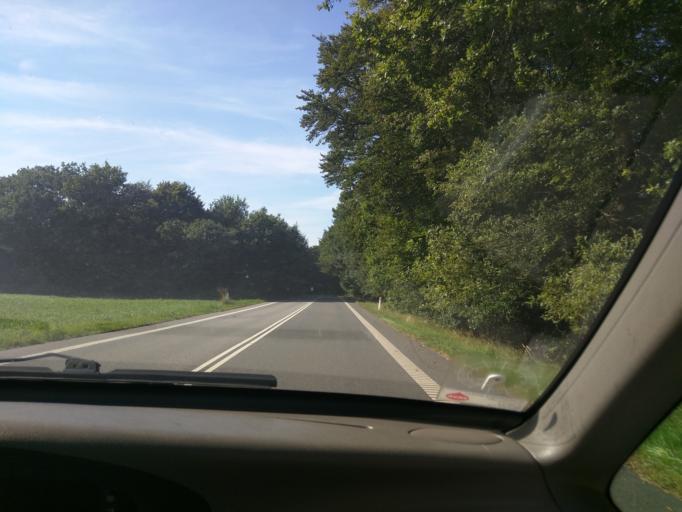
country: DK
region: Central Jutland
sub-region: Viborg Kommune
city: Bjerringbro
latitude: 56.4367
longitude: 9.6479
